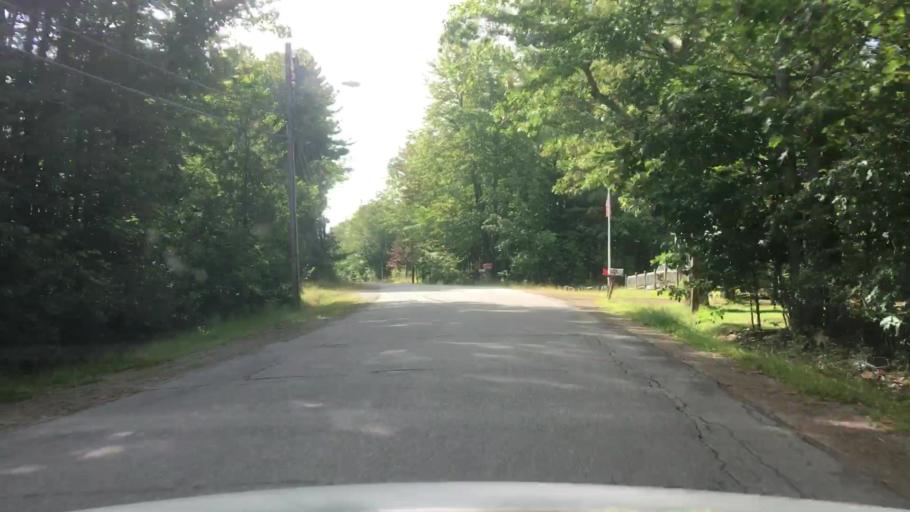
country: US
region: Maine
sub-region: Kennebec County
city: Gardiner
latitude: 44.1792
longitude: -69.8247
